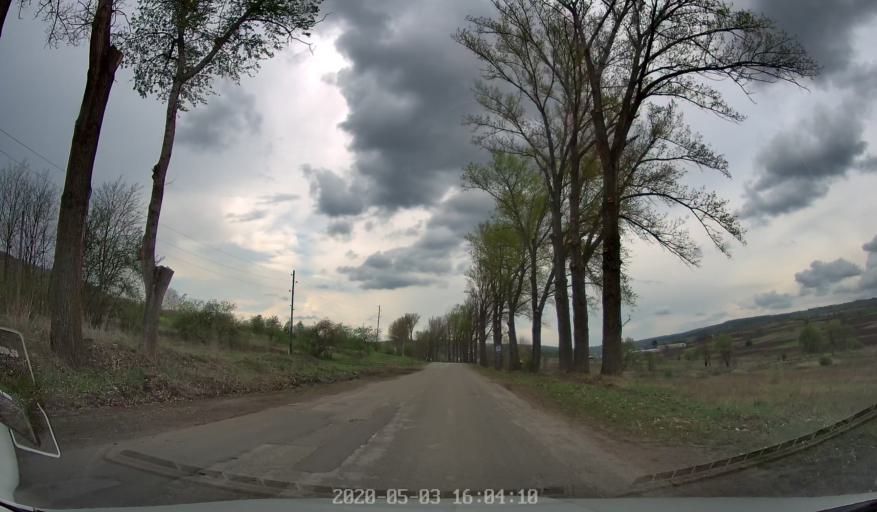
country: MD
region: Stinga Nistrului
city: Bucovat
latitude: 47.1848
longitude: 28.3714
